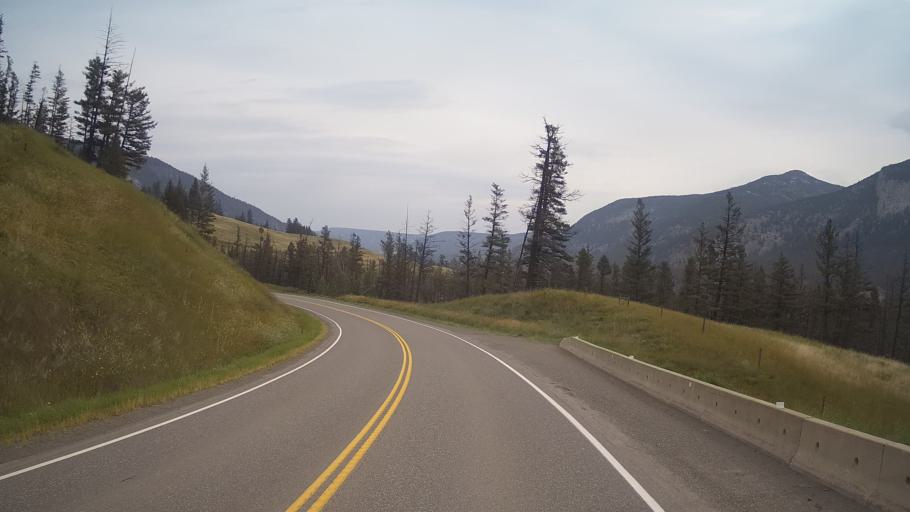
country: CA
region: British Columbia
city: Williams Lake
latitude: 51.9663
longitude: -122.2861
